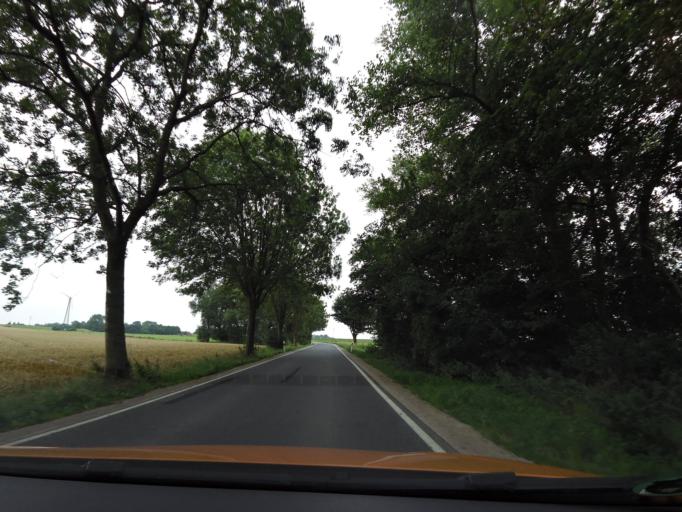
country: DE
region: Lower Saxony
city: Wirdum
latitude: 53.5054
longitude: 7.1551
